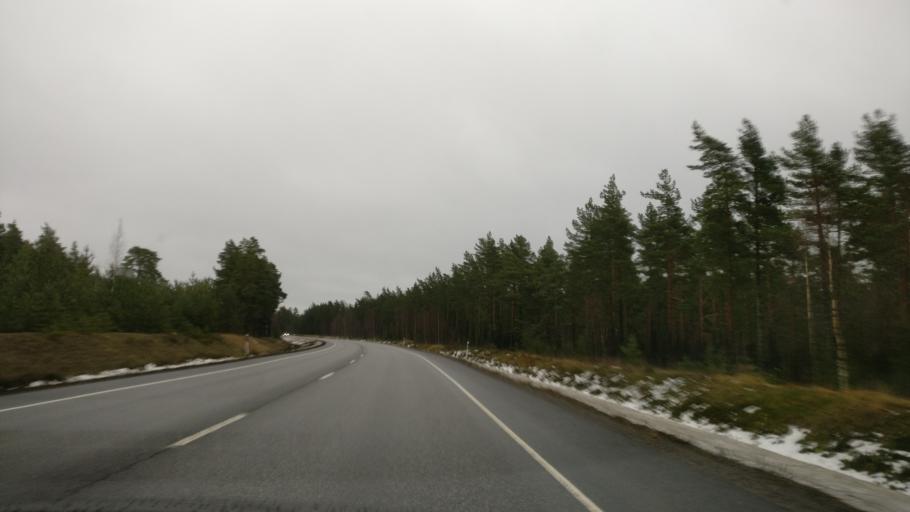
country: FI
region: Uusimaa
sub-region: Raaseporin
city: Hanko
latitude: 59.8606
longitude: 23.0426
